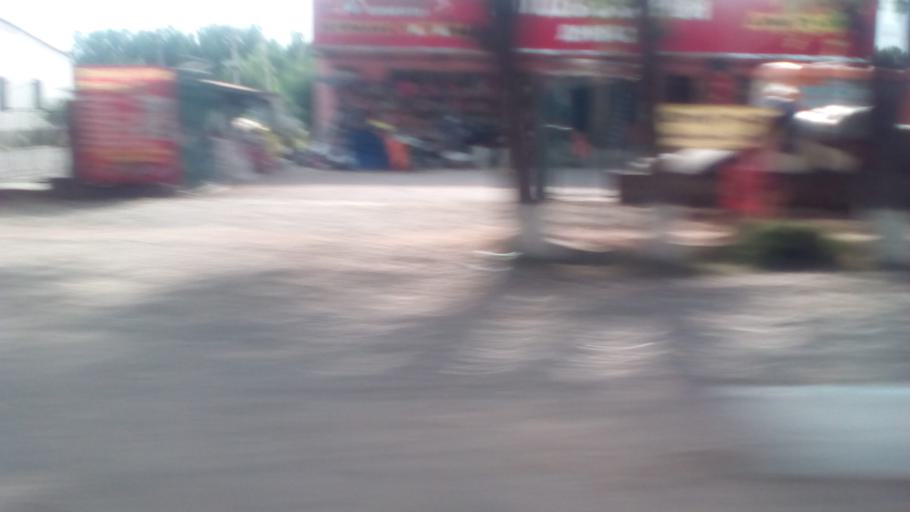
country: KZ
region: Ongtustik Qazaqstan
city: Shayan
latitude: 43.0430
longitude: 69.3898
